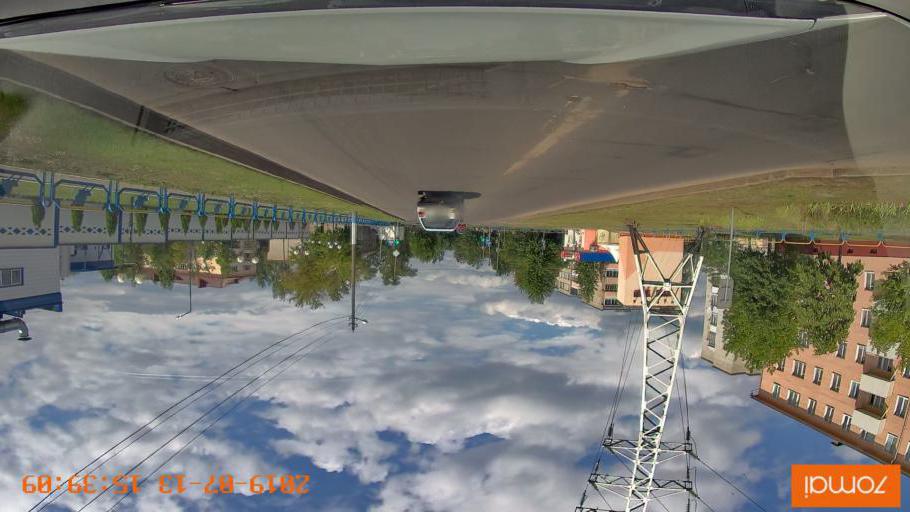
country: BY
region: Mogilev
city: Babruysk
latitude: 53.1358
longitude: 29.1779
